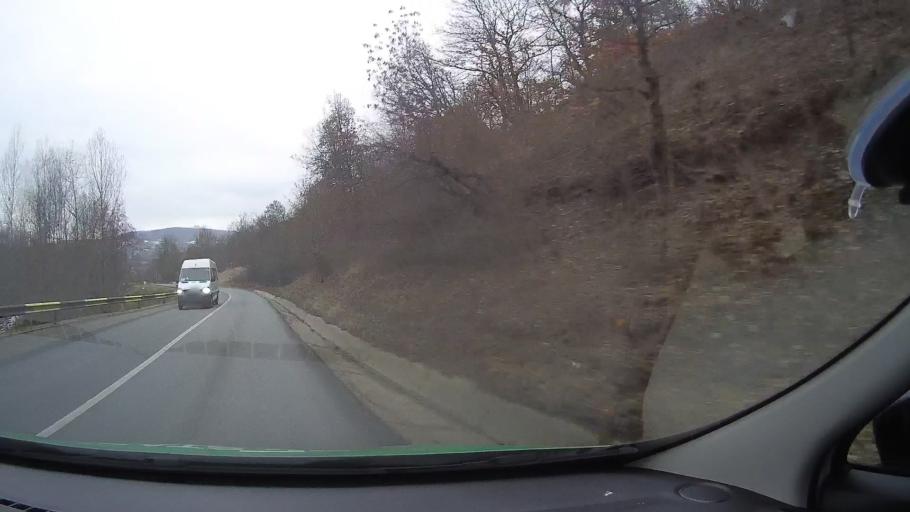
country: RO
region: Alba
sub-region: Comuna Metes
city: Metes
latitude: 46.1050
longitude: 23.4505
